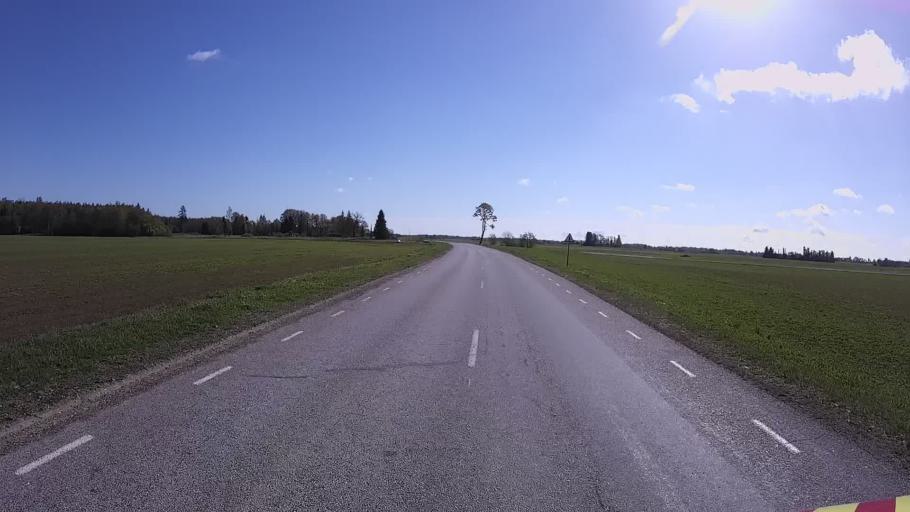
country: EE
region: Jaervamaa
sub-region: Jaerva-Jaani vald
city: Jarva-Jaani
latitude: 58.9057
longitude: 25.8297
